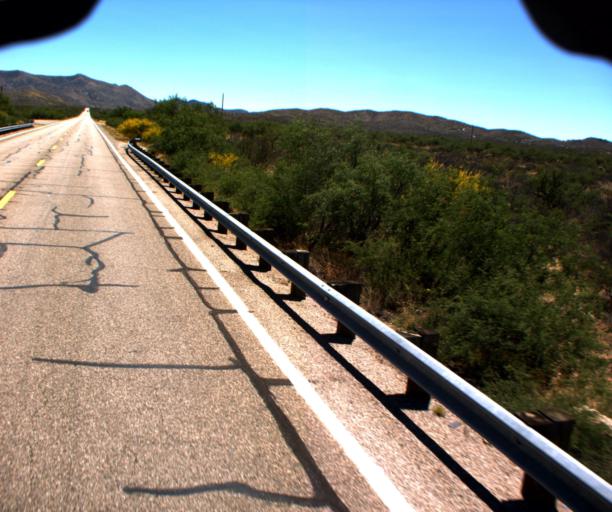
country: US
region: Arizona
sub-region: Pima County
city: Vail
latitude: 31.9472
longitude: -110.6655
